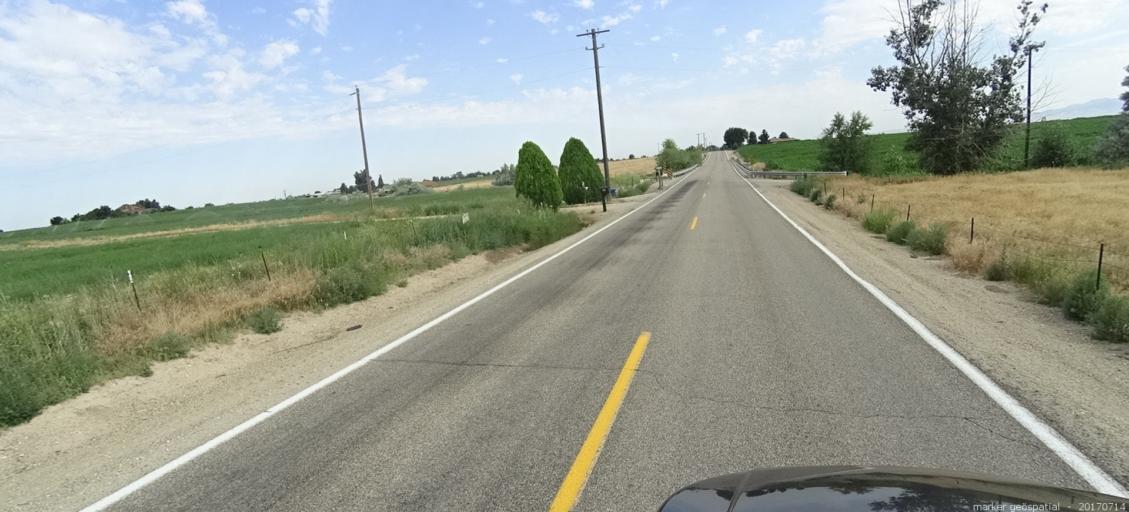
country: US
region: Idaho
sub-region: Ada County
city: Kuna
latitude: 43.4624
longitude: -116.3546
